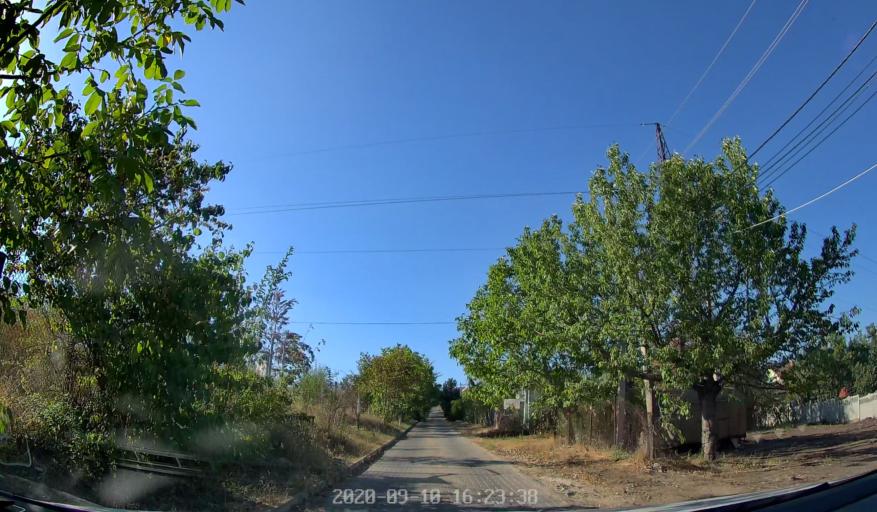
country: MD
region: Chisinau
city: Stauceni
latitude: 47.0518
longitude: 28.9232
